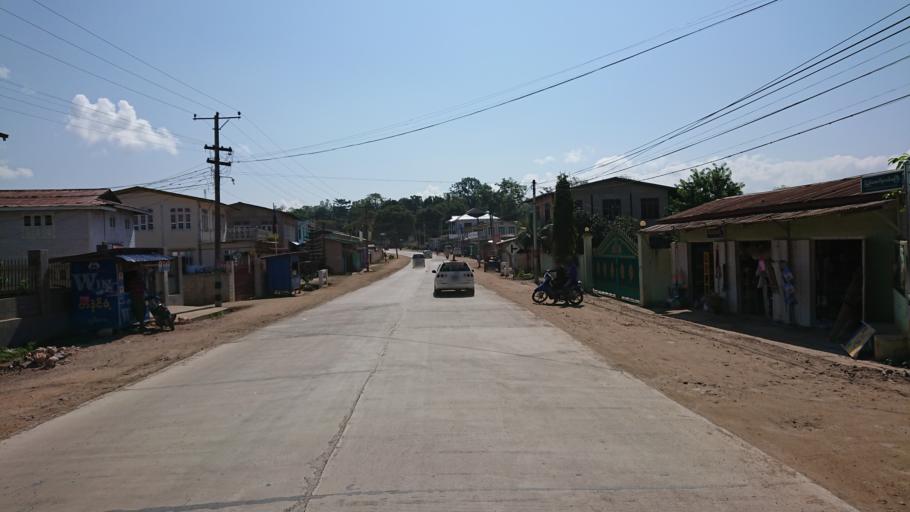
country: MM
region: Shan
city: Taunggyi
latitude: 20.8017
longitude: 97.1787
